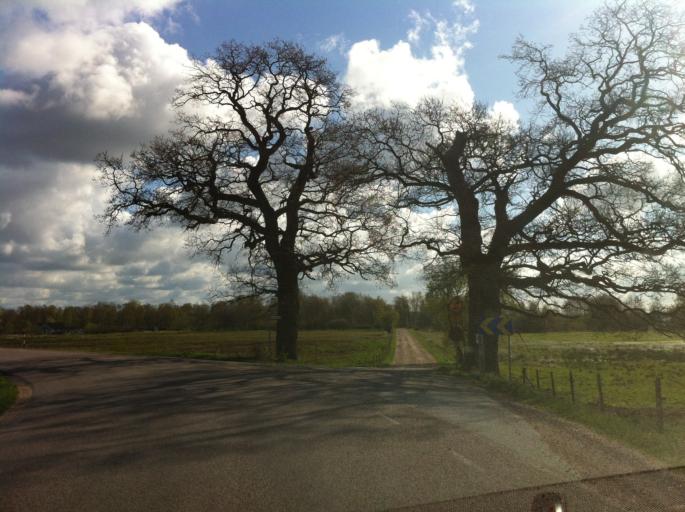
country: SE
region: Skane
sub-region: Eslovs Kommun
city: Stehag
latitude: 55.9015
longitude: 13.4294
